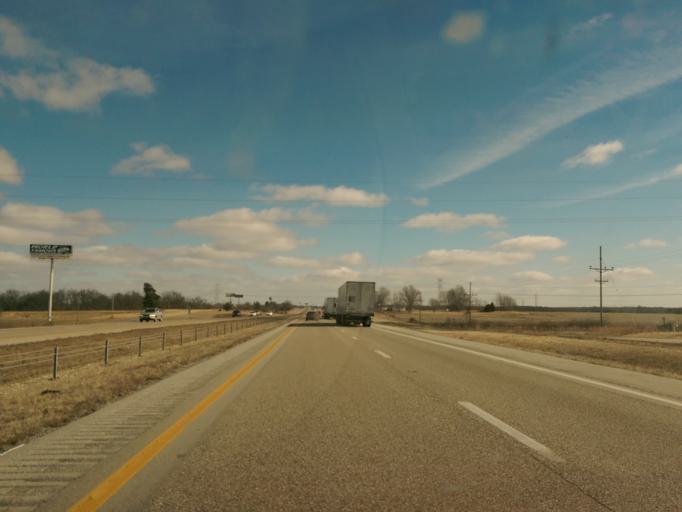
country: US
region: Missouri
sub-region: Montgomery County
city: Montgomery City
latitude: 38.9046
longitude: -91.4957
